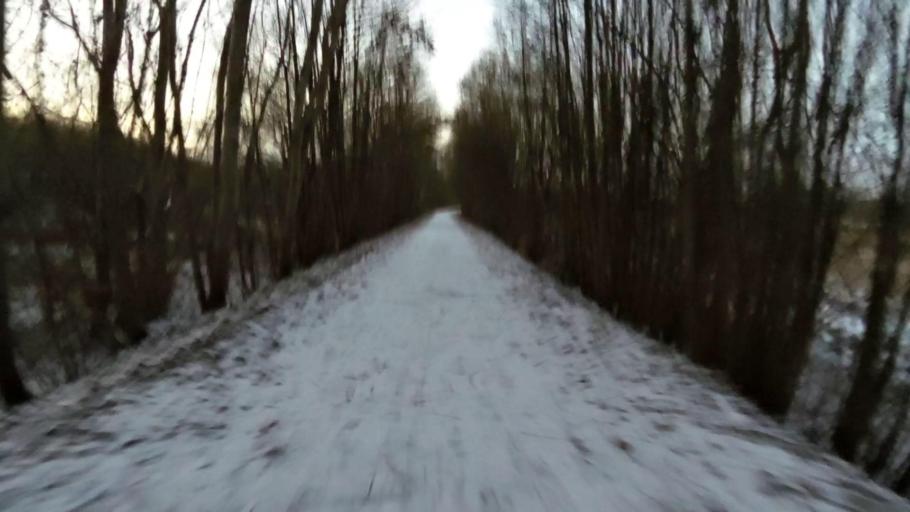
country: PL
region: West Pomeranian Voivodeship
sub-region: Powiat swidwinski
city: Polczyn-Zdroj
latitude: 53.7515
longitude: 16.0593
